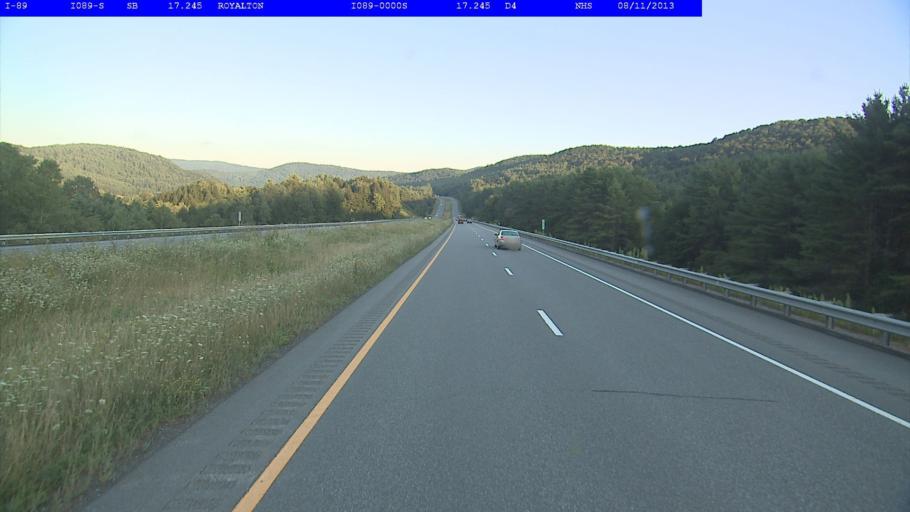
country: US
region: Vermont
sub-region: Windsor County
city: Woodstock
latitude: 43.8045
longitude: -72.5150
